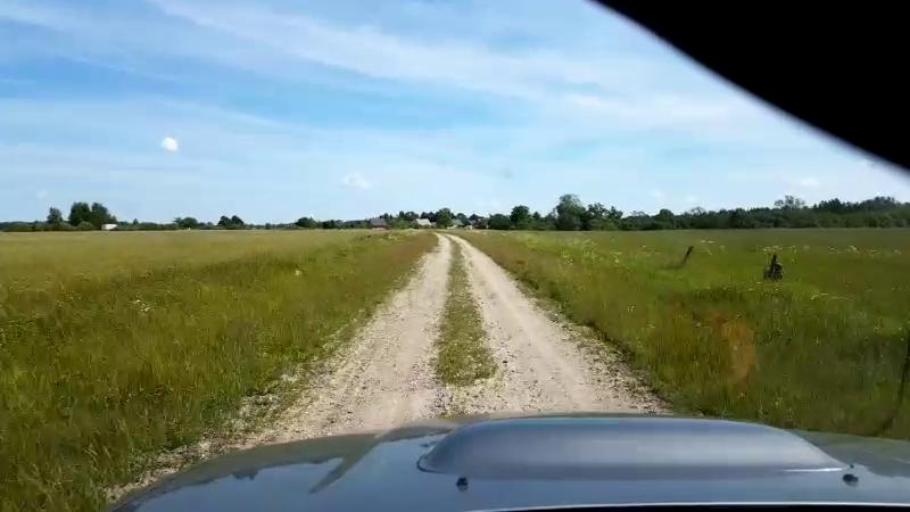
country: EE
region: Paernumaa
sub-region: Sauga vald
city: Sauga
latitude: 58.5039
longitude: 24.5466
